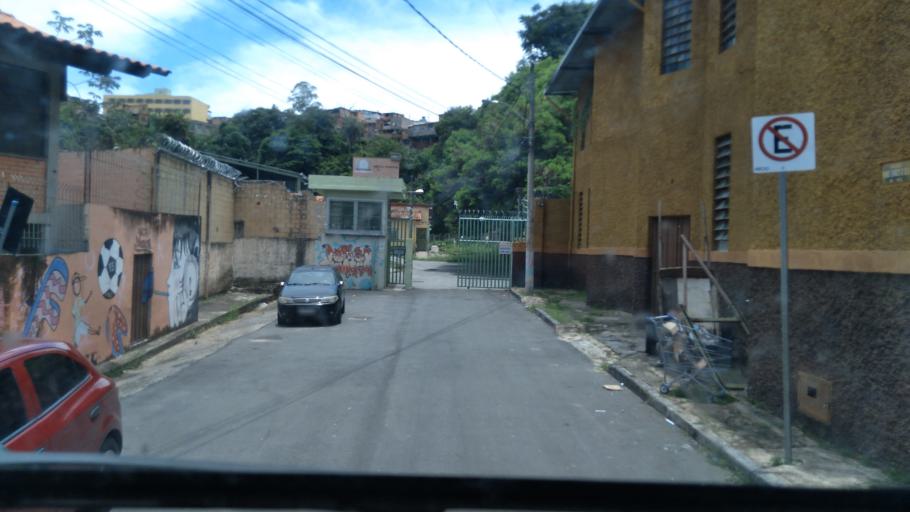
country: BR
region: Minas Gerais
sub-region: Belo Horizonte
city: Belo Horizonte
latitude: -19.9139
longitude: -43.9065
